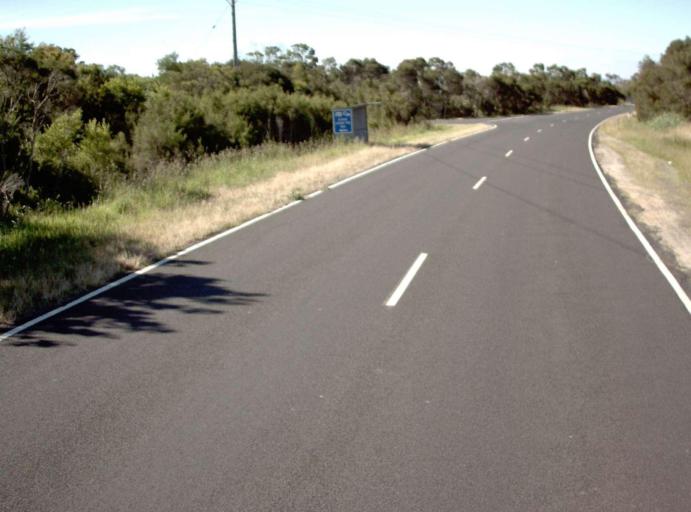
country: AU
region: Victoria
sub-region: Latrobe
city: Traralgon
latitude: -38.6427
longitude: 146.6712
